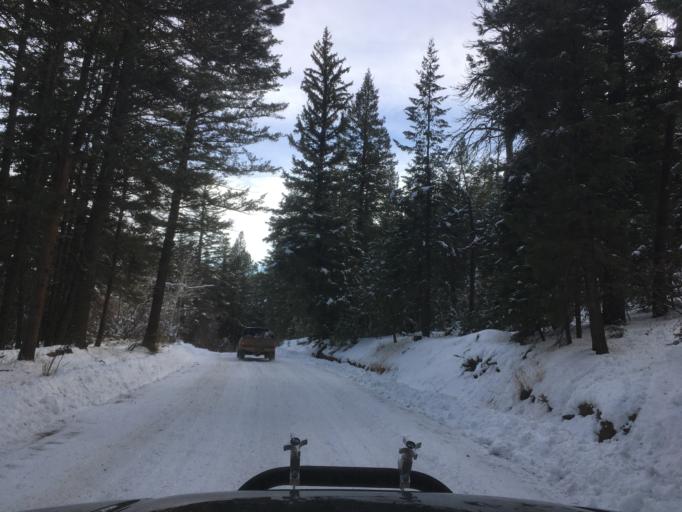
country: US
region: Wyoming
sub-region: Albany County
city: Laramie
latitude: 40.9186
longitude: -105.5093
